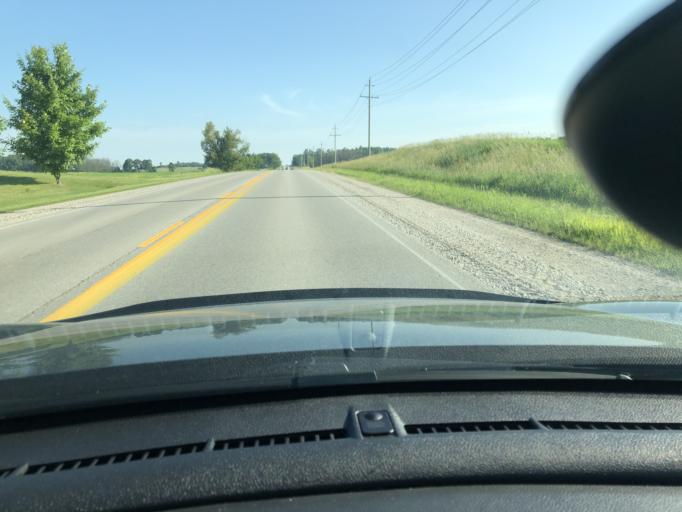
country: CA
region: Ontario
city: Stratford
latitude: 43.3903
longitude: -80.8373
